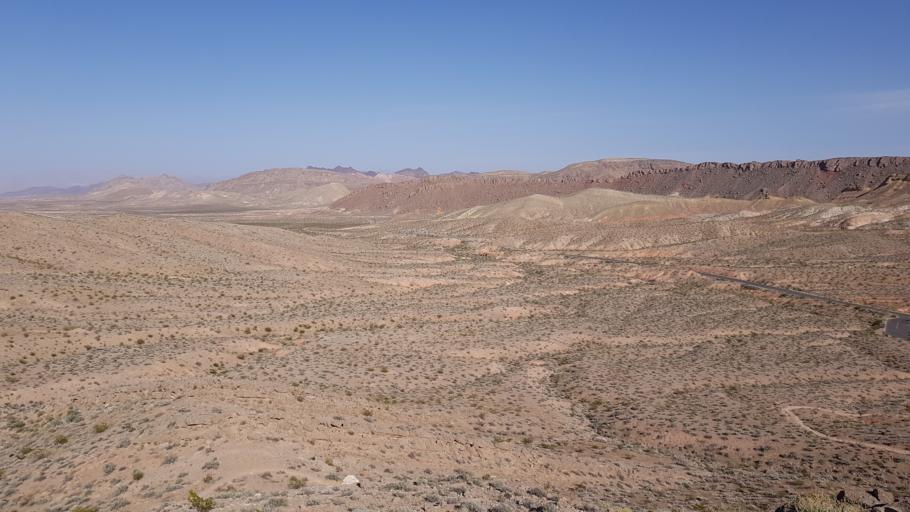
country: US
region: Nevada
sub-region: Clark County
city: Boulder City
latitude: 36.2293
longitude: -114.6238
